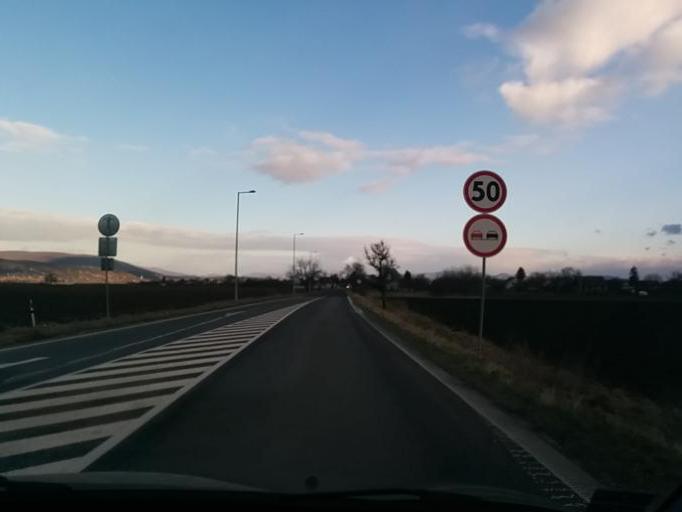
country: SK
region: Nitriansky
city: Cachtice
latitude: 48.6957
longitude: 17.8484
